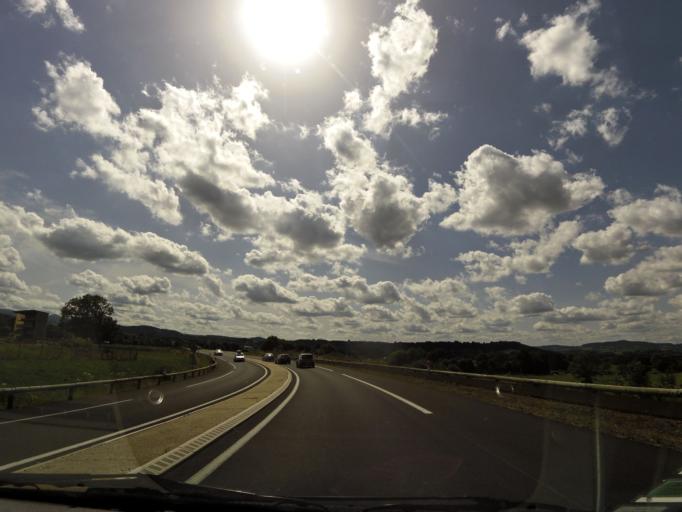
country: FR
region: Auvergne
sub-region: Departement du Puy-de-Dome
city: Aydat
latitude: 45.7289
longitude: 2.8914
